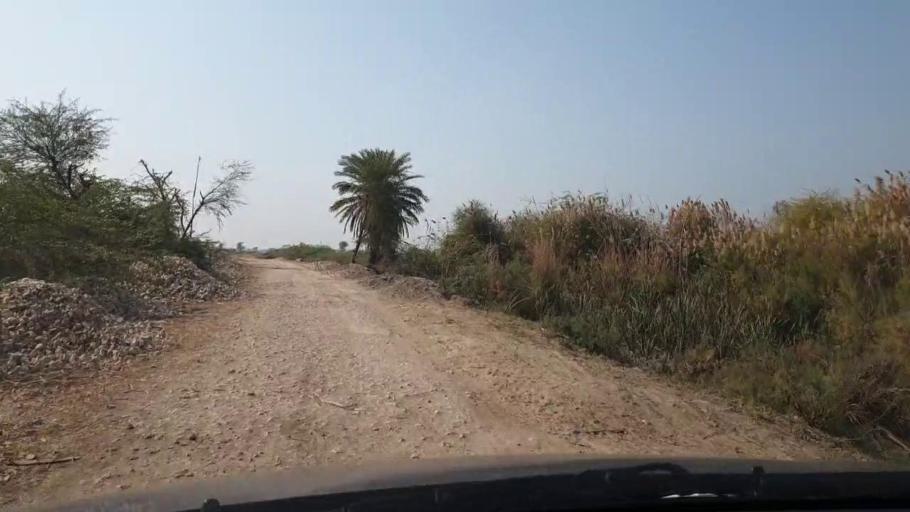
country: PK
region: Sindh
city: Jhol
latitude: 25.8975
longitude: 69.0080
